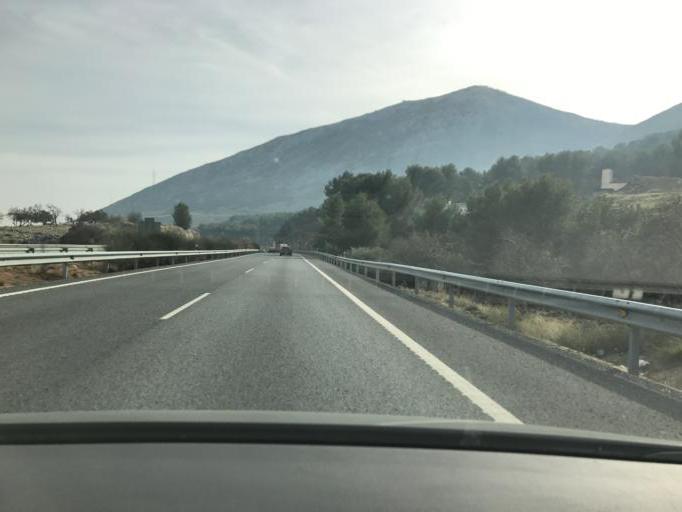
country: ES
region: Andalusia
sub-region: Provincia de Granada
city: Loja
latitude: 37.1630
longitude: -4.1587
